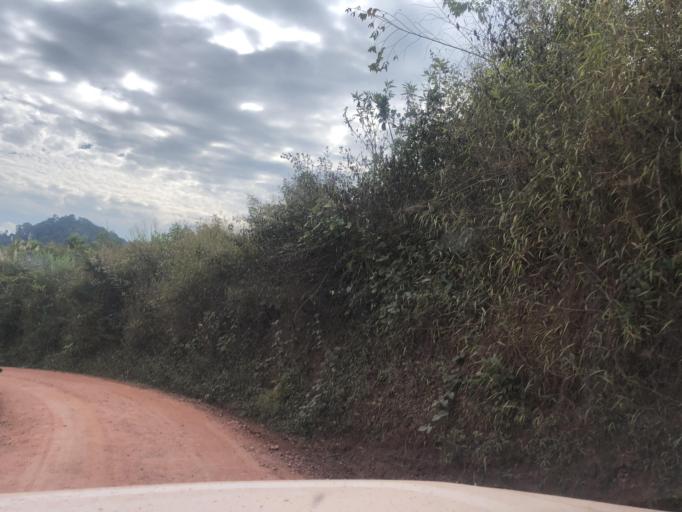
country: CN
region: Yunnan
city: Menglie
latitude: 22.1201
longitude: 101.7401
